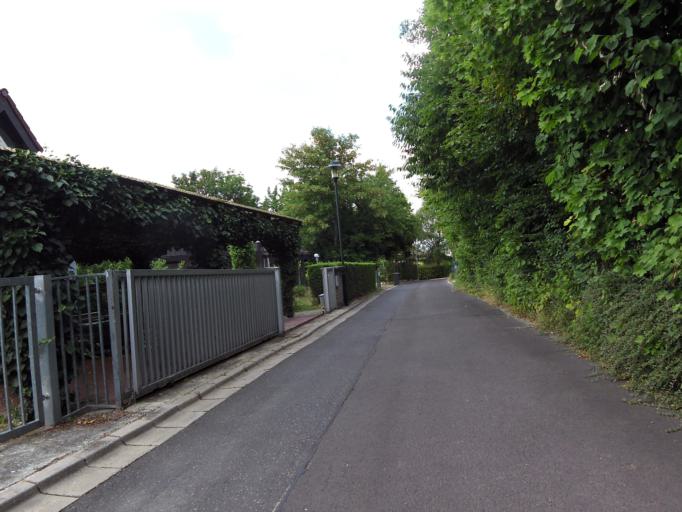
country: DE
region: Bavaria
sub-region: Regierungsbezirk Unterfranken
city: Gerbrunn
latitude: 49.7845
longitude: 10.0015
